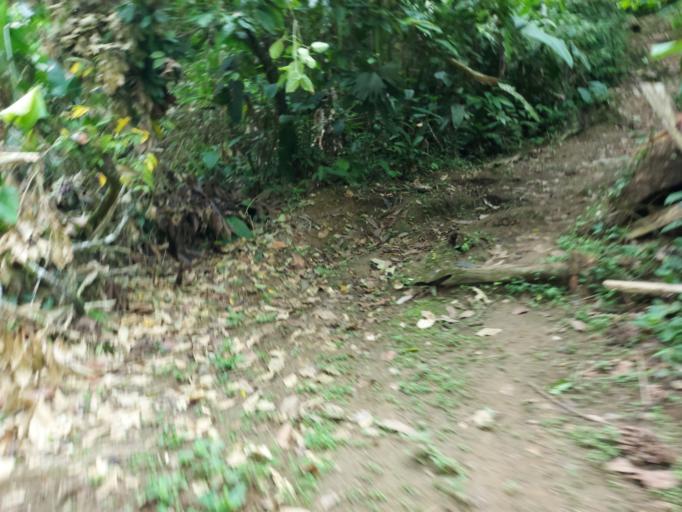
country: PA
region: Bocas del Toro
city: Barranco
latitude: 9.6426
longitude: -82.7851
